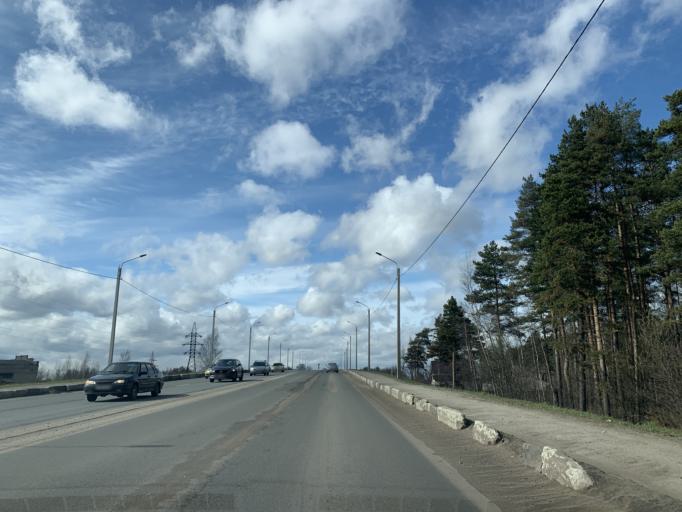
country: RU
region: Jaroslavl
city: Yaroslavl
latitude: 57.6627
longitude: 39.9564
